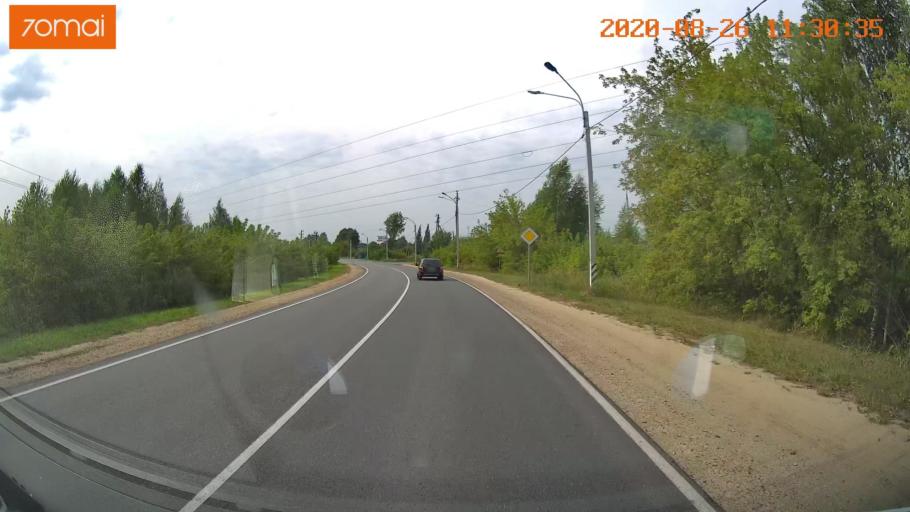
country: RU
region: Rjazan
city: Shilovo
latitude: 54.3146
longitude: 40.8812
